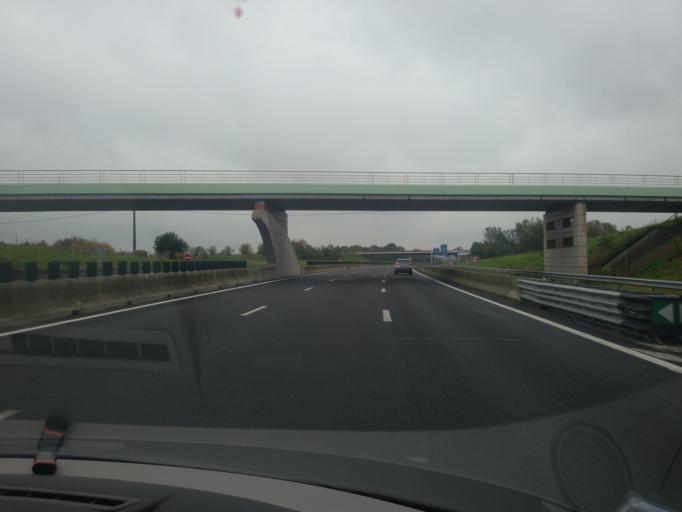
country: FR
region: Haute-Normandie
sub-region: Departement de l'Eure
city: Beuzeville
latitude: 49.3167
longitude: 0.3100
